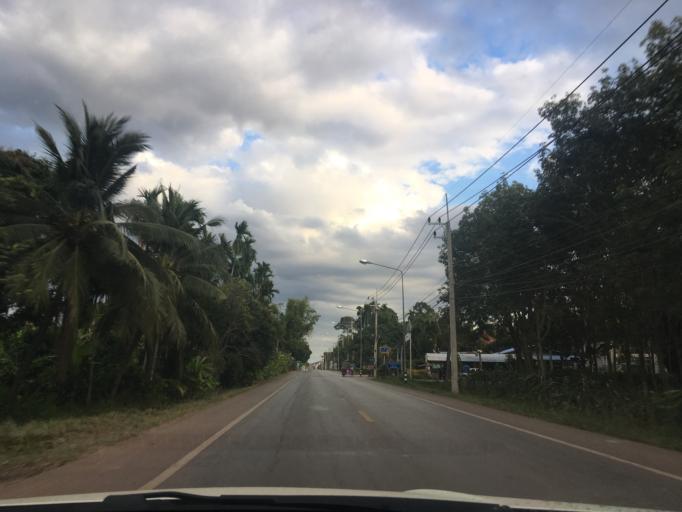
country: TH
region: Chanthaburi
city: Na Yai Am
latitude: 12.6920
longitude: 101.8094
